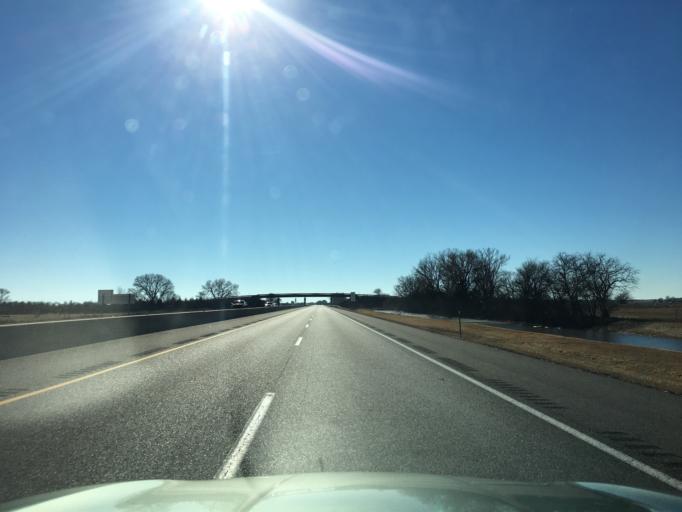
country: US
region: Kansas
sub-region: Sumner County
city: Mulvane
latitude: 37.4676
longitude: -97.3227
